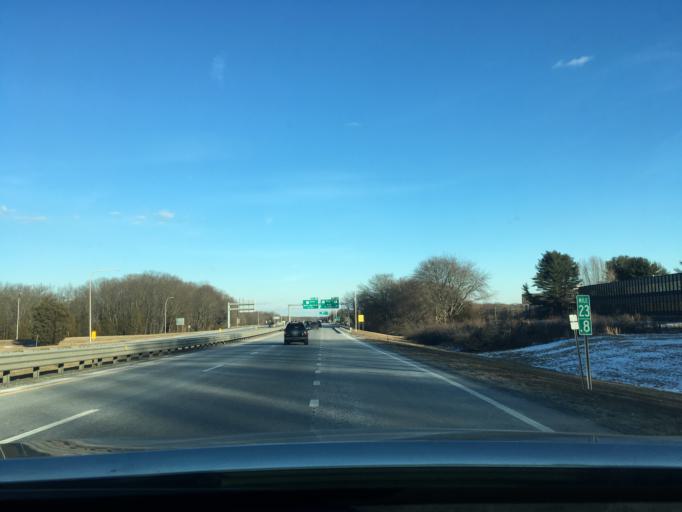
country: US
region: Rhode Island
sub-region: Kent County
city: West Warwick
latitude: 41.6664
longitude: -71.5040
